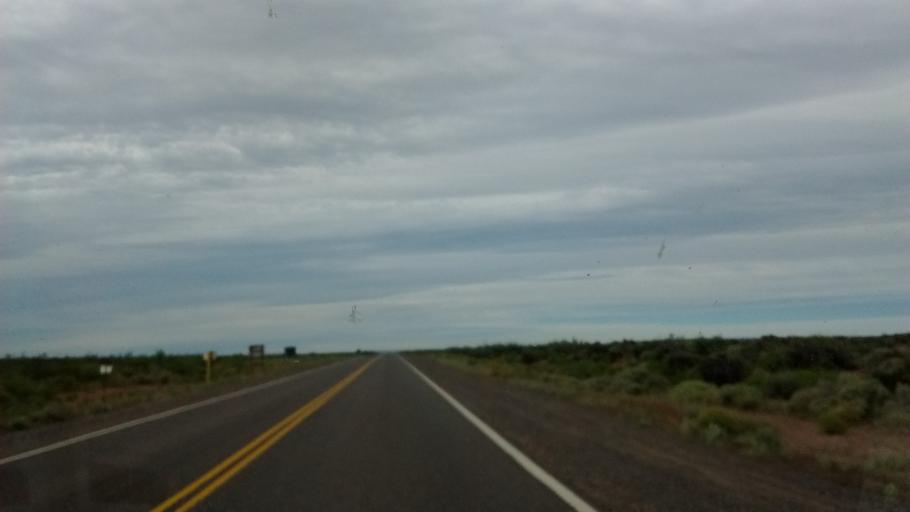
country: AR
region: Rio Negro
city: Catriel
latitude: -38.0543
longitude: -67.9204
